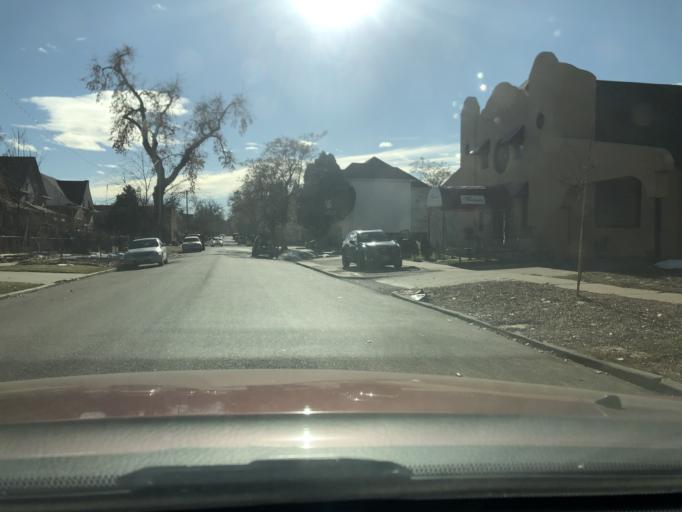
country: US
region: Colorado
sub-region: Denver County
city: Denver
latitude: 39.7542
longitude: -104.9746
